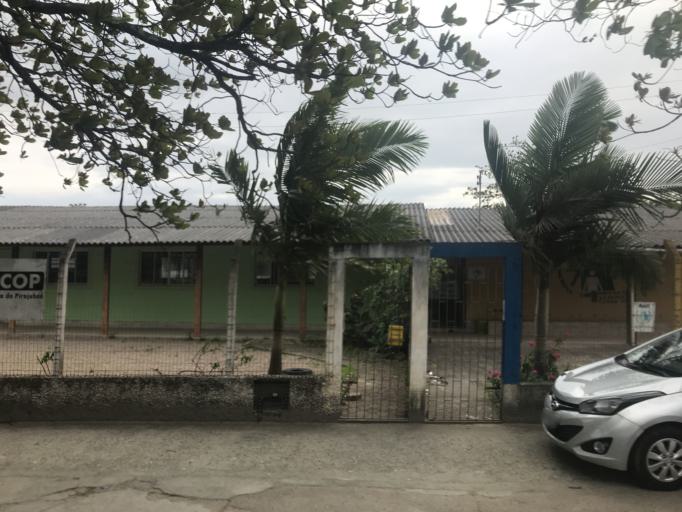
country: BR
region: Santa Catarina
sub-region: Florianopolis
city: Costeira do Pirajubae
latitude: -27.6304
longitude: -48.5240
